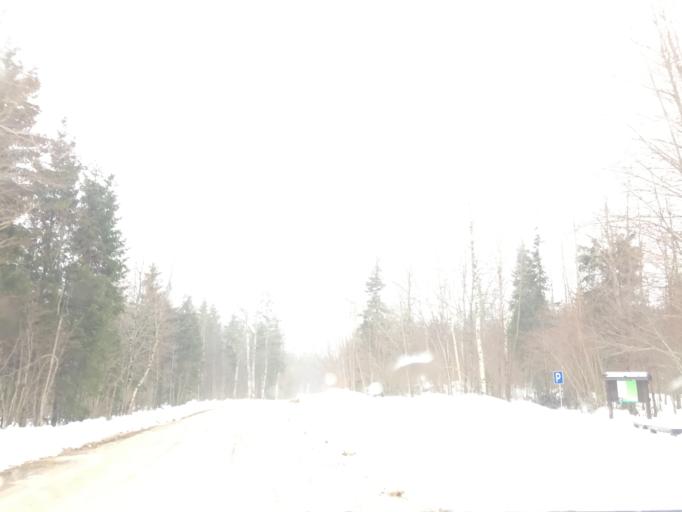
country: EE
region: Saare
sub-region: Kuressaare linn
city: Kuressaare
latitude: 58.2944
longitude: 22.1036
